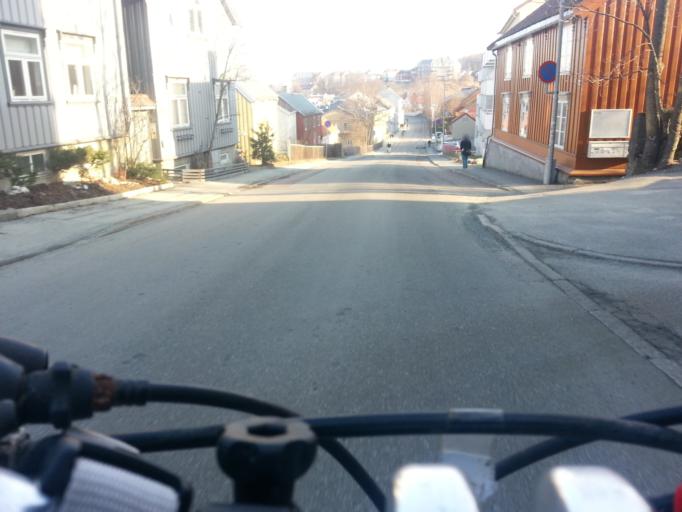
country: NO
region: Sor-Trondelag
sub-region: Trondheim
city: Trondheim
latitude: 63.4230
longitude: 10.4005
